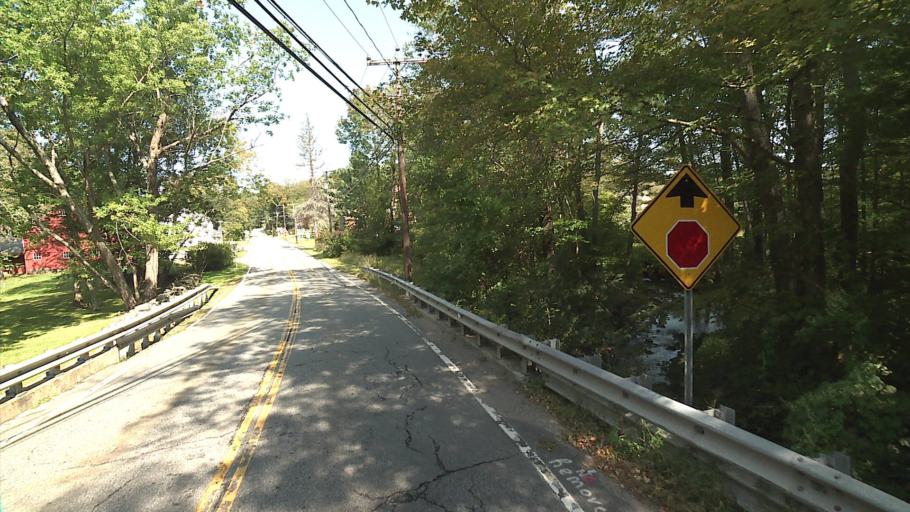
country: US
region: Connecticut
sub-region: Windham County
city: Quinebaug
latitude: 41.9908
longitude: -71.9969
